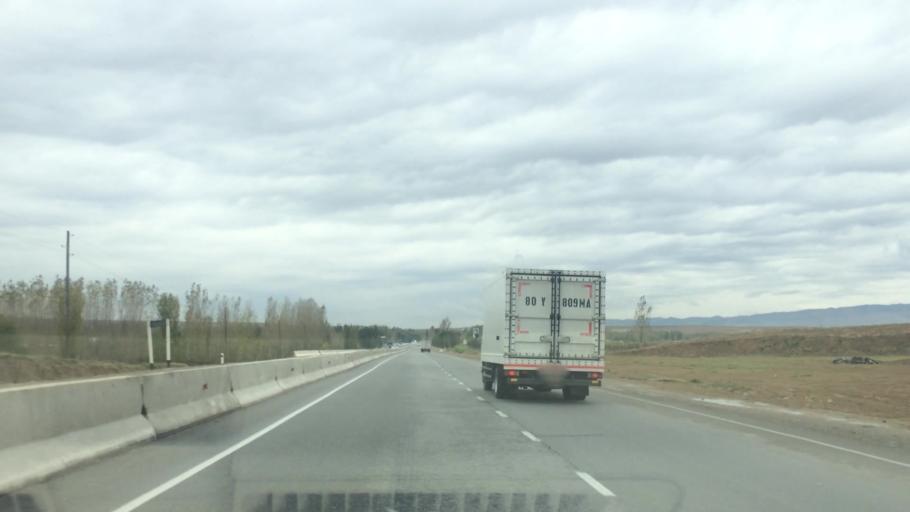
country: UZ
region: Jizzax
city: Jizzax
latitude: 39.9670
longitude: 67.5533
